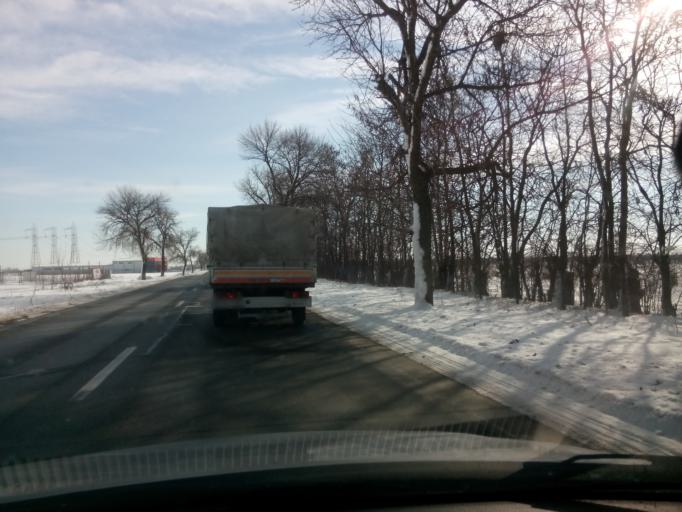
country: RO
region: Ilfov
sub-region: Comuna Glina
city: Glina
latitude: 44.3246
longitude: 26.2622
